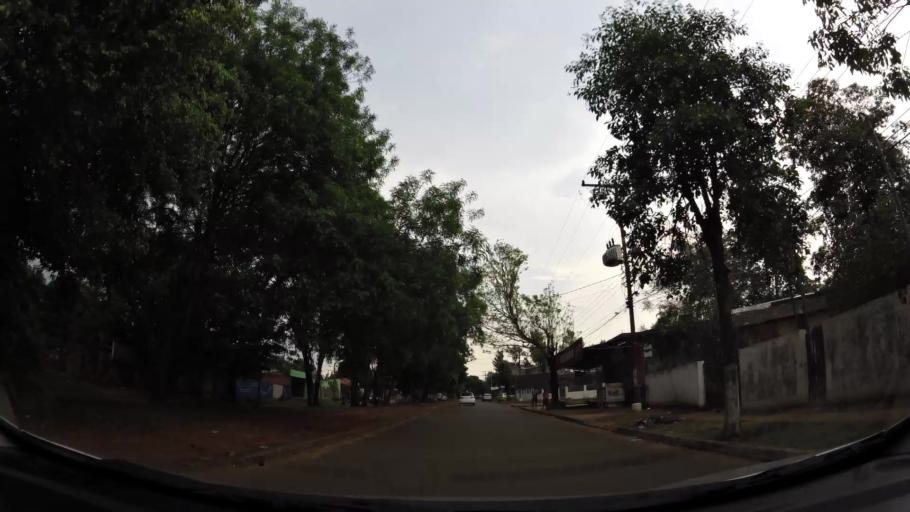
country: BR
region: Parana
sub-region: Foz Do Iguacu
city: Foz do Iguacu
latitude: -25.5419
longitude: -54.6018
